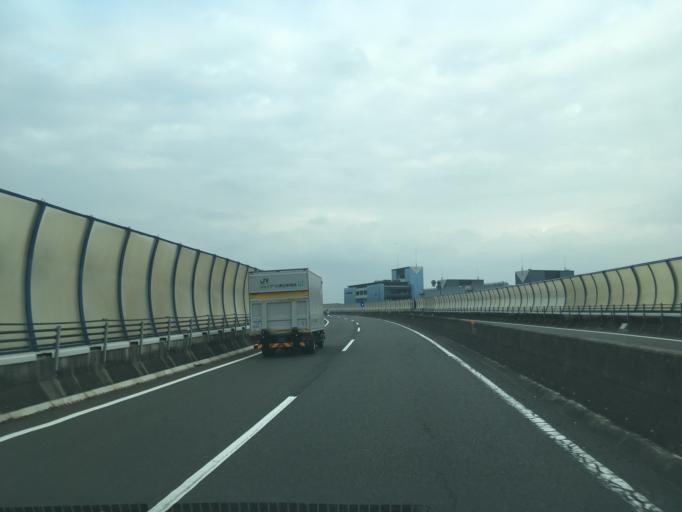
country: JP
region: Kanagawa
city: Chigasaki
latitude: 35.3293
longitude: 139.3813
